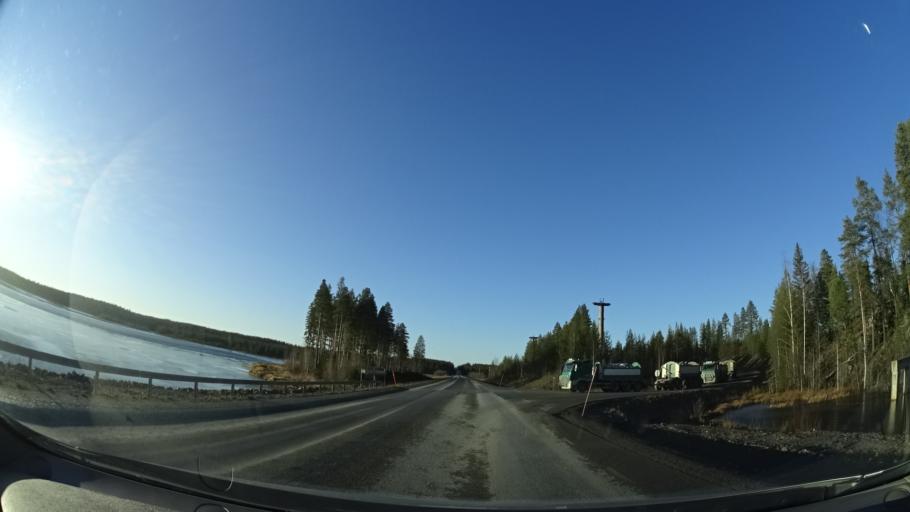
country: SE
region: Vaesterbotten
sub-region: Skelleftea Kommun
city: Langsele
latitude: 64.8838
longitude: 20.2971
